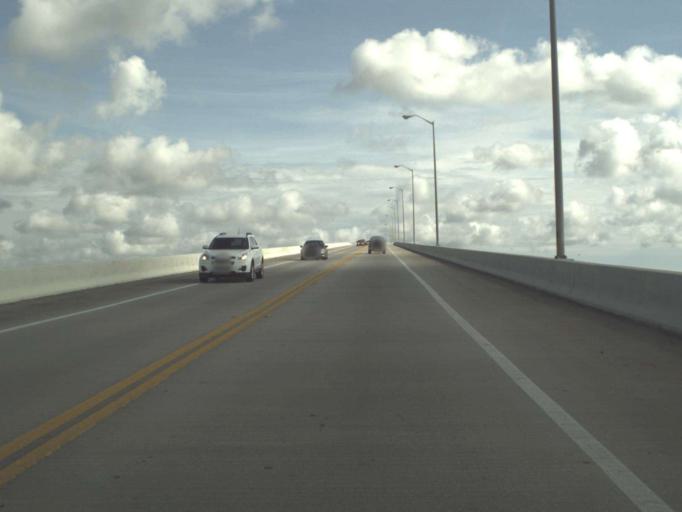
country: US
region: Florida
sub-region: Gulf County
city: Port Saint Joe
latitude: 29.8351
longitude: -85.3151
